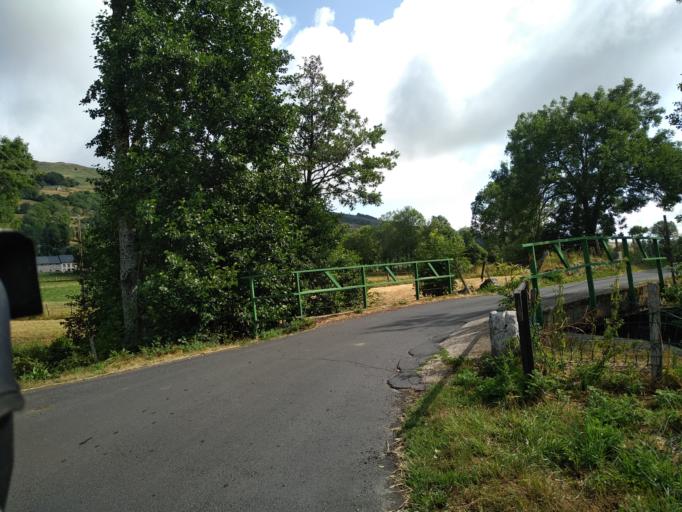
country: FR
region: Auvergne
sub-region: Departement du Cantal
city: Murat
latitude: 45.1345
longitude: 2.7454
